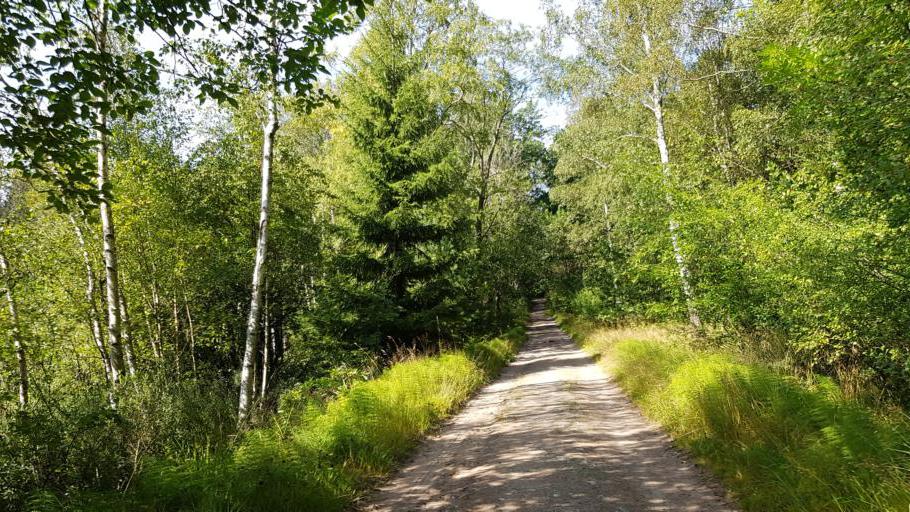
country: SE
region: Vaestra Goetaland
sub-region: Harryda Kommun
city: Molnlycke
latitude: 57.6750
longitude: 12.0705
